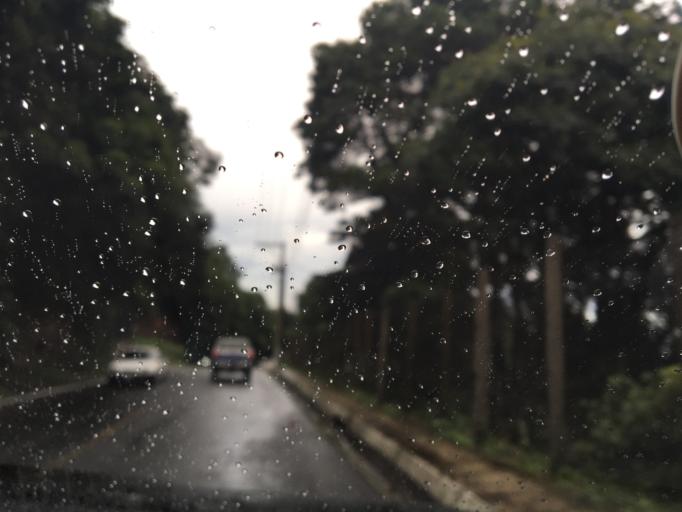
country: GT
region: Guatemala
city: Santa Catarina Pinula
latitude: 14.5540
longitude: -90.4935
